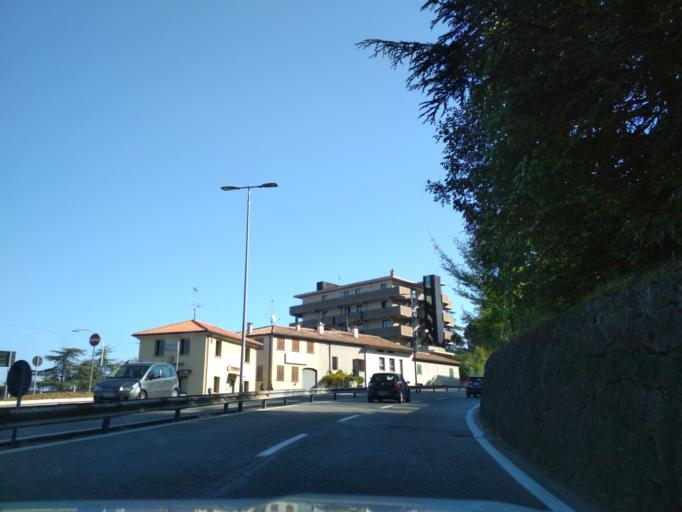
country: SM
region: Borgo Maggiore
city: Borgo Maggiore
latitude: 43.9410
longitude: 12.4447
